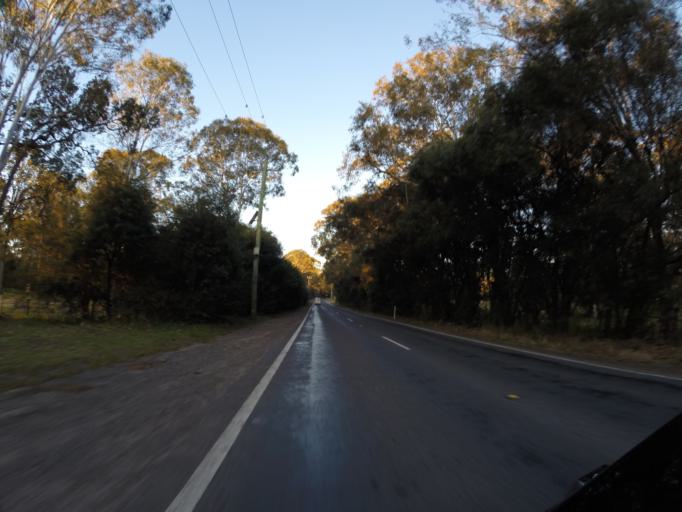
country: AU
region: New South Wales
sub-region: Camden
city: Cobbitty
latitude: -34.0159
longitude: 150.6946
